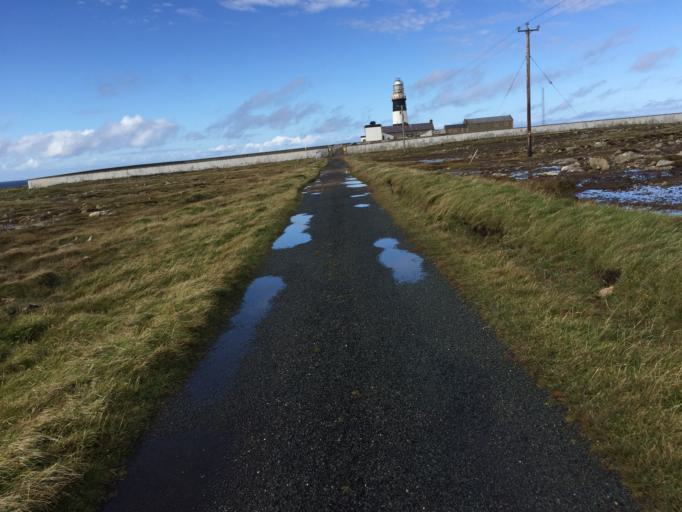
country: IE
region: Ulster
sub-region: County Donegal
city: Derrybeg
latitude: 55.2704
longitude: -8.2481
